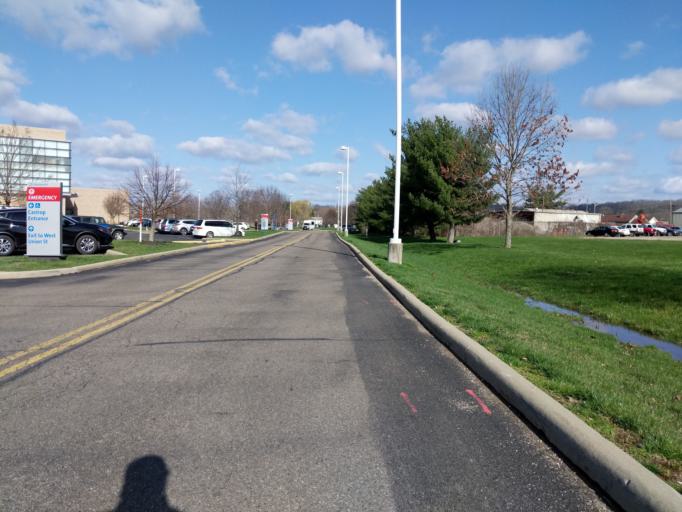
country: US
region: Ohio
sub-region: Athens County
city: Athens
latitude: 39.3281
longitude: -82.1143
